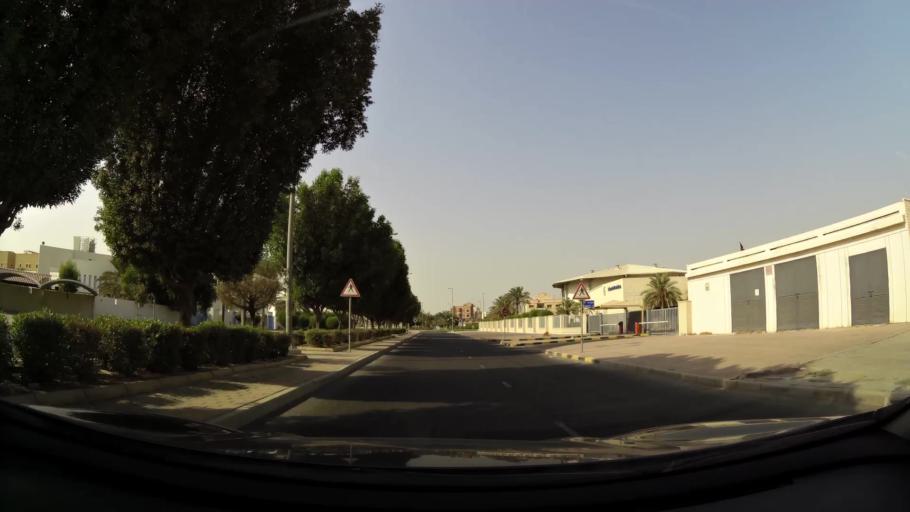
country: KW
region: Mubarak al Kabir
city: Sabah as Salim
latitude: 29.2744
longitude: 48.0491
